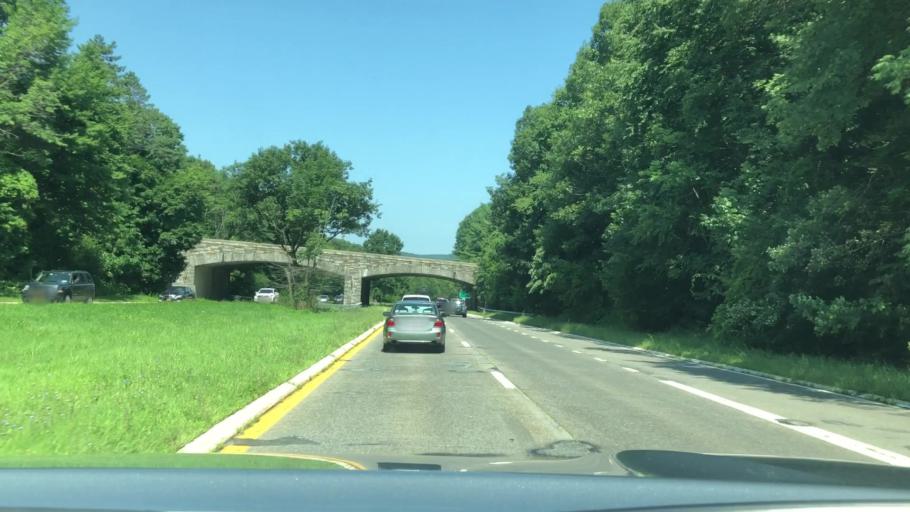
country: US
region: New York
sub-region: Rockland County
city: Pomona
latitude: 41.1712
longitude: -74.0320
